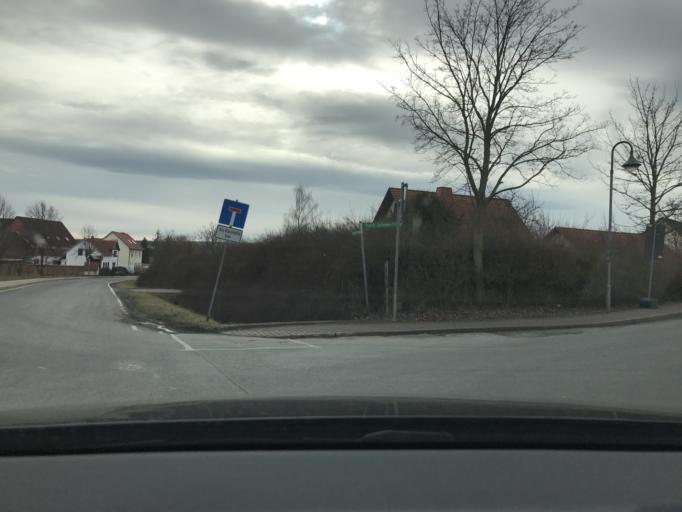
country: DE
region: Thuringia
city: Helmsdorf
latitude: 51.2582
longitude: 10.3967
